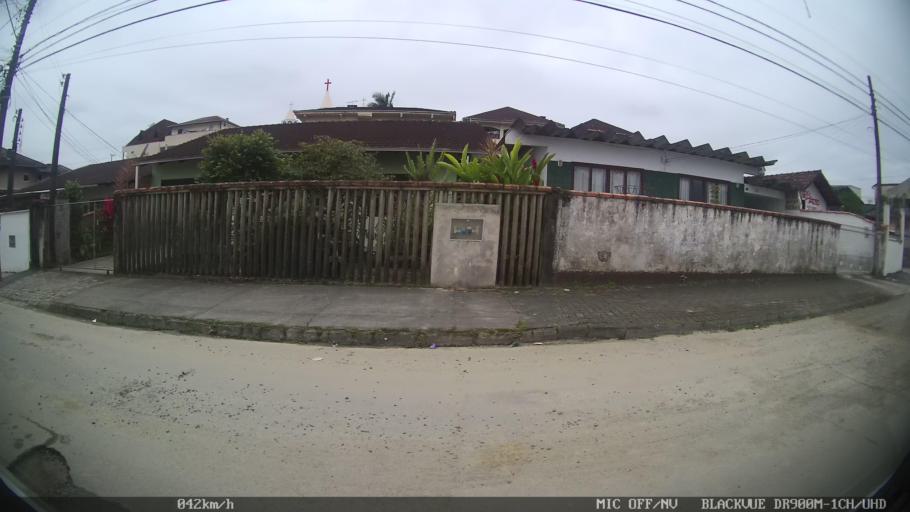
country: BR
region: Santa Catarina
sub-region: Joinville
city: Joinville
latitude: -26.2674
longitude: -48.8872
